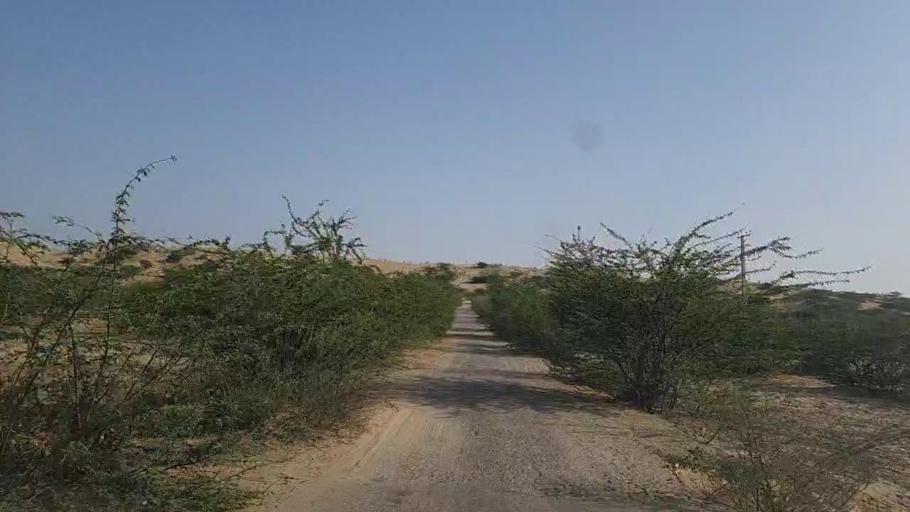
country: PK
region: Sindh
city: Naukot
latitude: 24.6202
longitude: 69.3714
